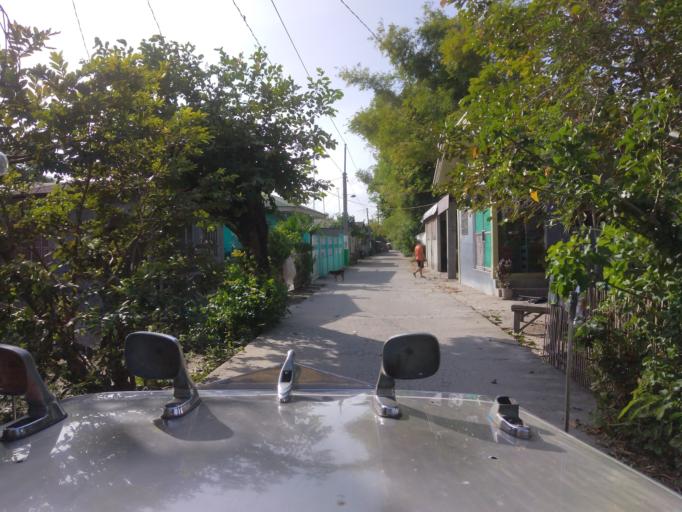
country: PH
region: Central Luzon
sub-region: Province of Pampanga
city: Malino
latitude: 15.1005
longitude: 120.6931
